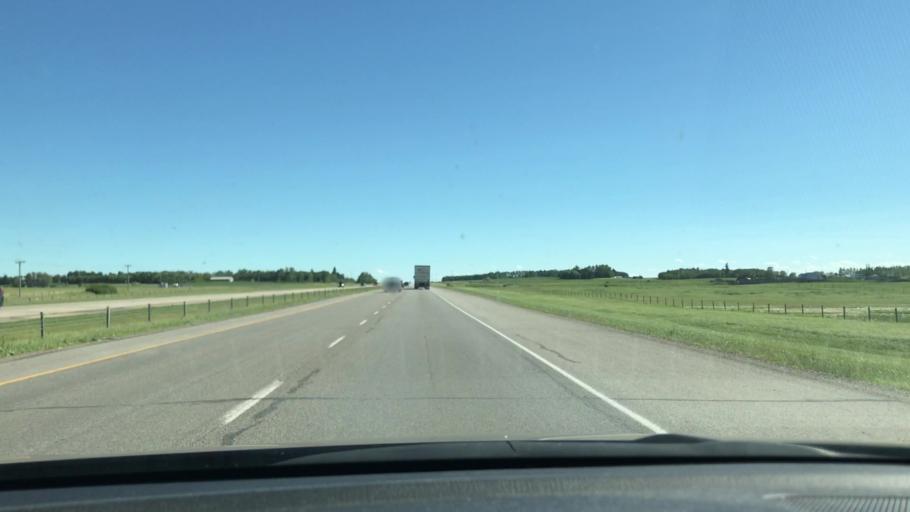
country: CA
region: Alberta
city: Olds
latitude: 51.8955
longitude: -114.0249
